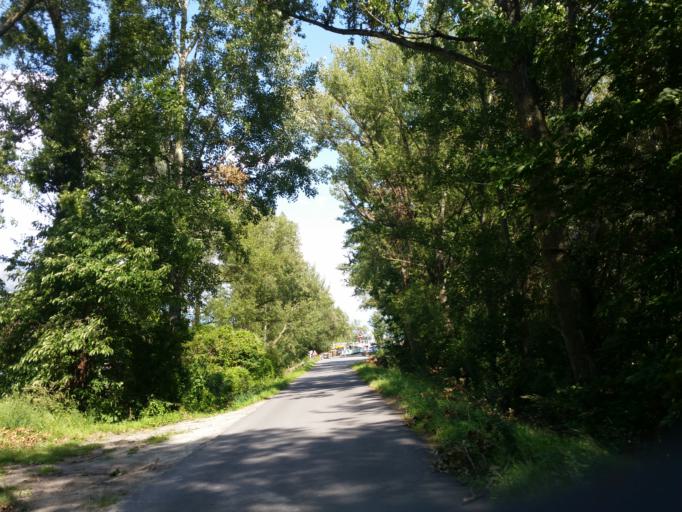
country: CH
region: Valais
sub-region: Martigny District
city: Charrat-les-Chenes
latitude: 46.1468
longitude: 7.1481
